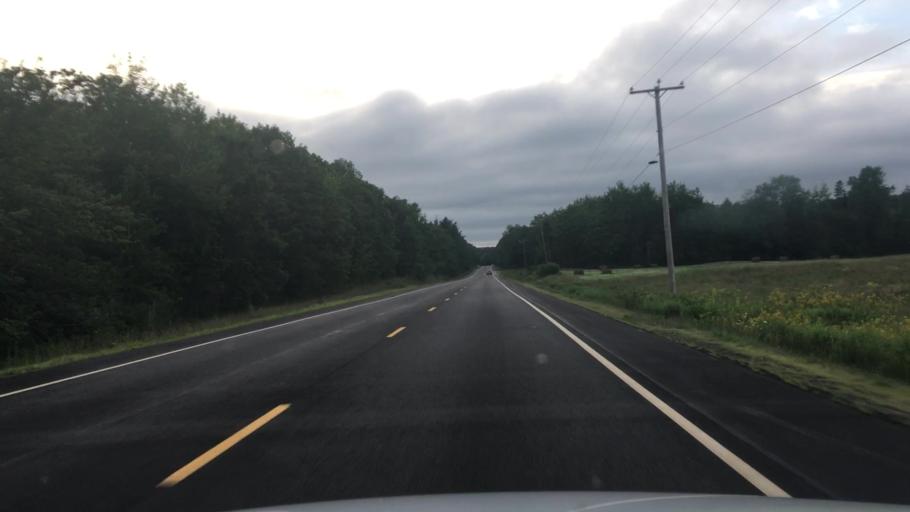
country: US
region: Maine
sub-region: Waldo County
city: Searsmont
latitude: 44.4032
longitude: -69.1657
